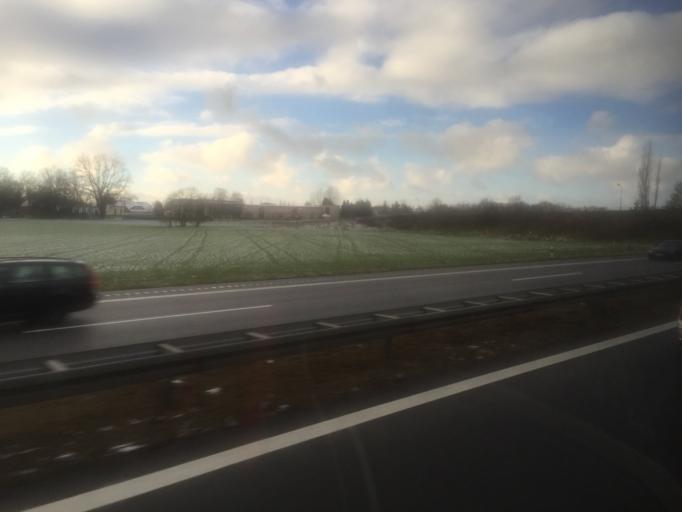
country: DE
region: Brandenburg
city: Walsleben
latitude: 52.9429
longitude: 12.6732
